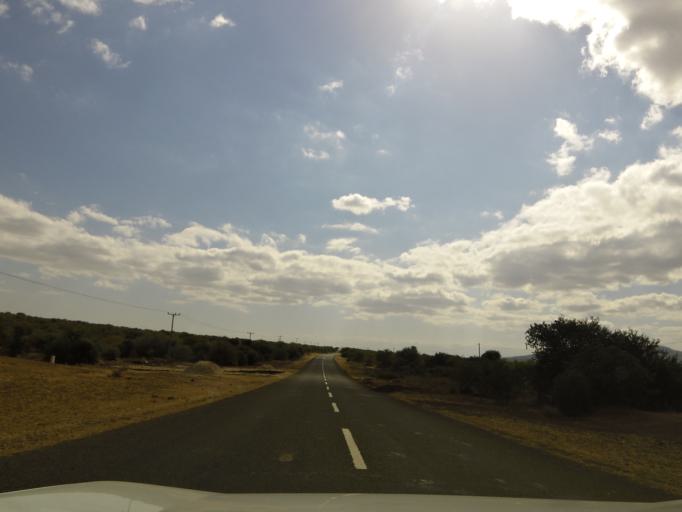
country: TZ
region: Arusha
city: Mto wa Mbu
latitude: -3.5270
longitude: 36.0615
